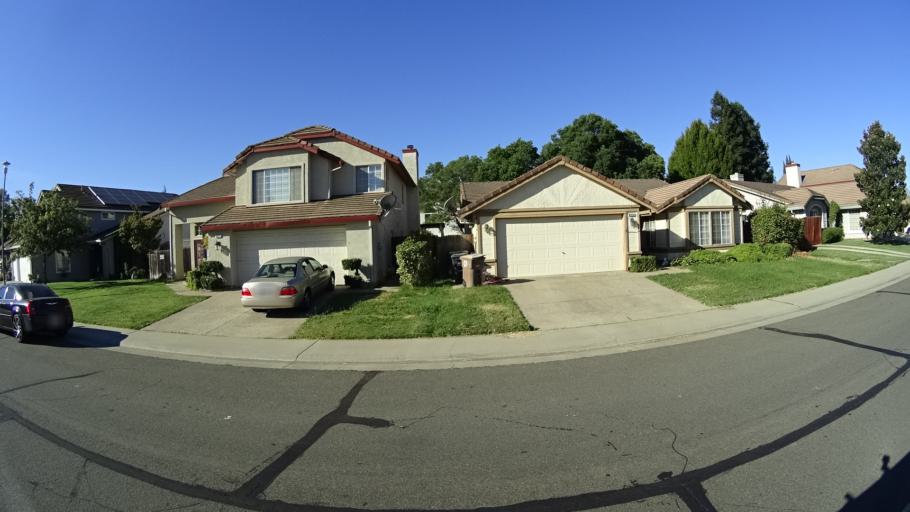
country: US
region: California
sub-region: Sacramento County
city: Elk Grove
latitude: 38.4346
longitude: -121.3763
